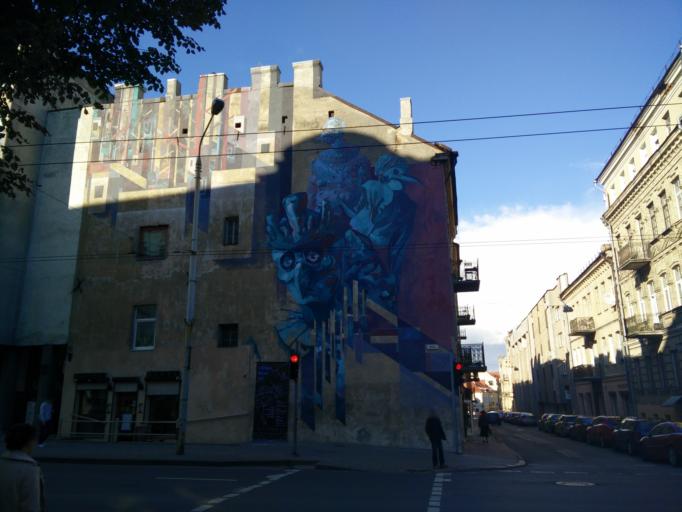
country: LT
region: Vilnius County
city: Naujamiestis
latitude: 54.6723
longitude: 25.2798
